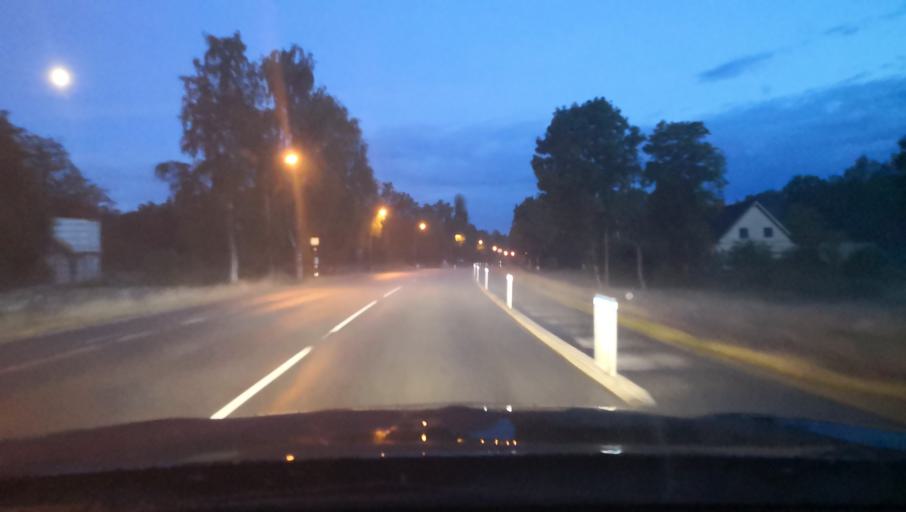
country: SE
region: Skane
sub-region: Osby Kommun
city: Osby
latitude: 56.3625
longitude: 13.9800
